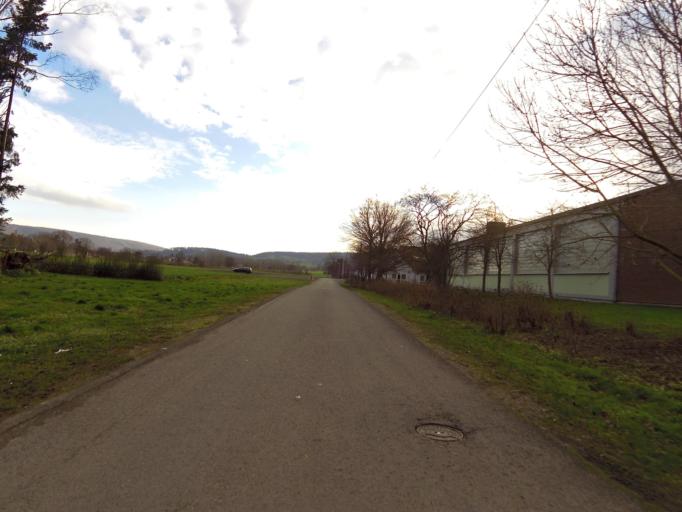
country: DE
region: Lower Saxony
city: Buhren
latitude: 51.4867
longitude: 9.6039
